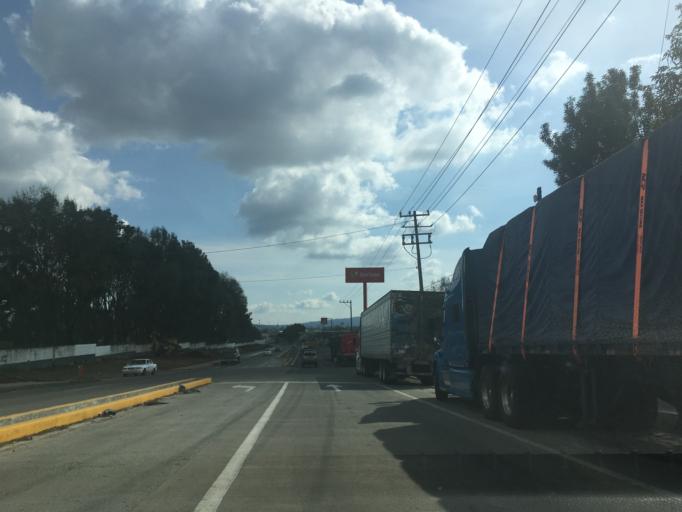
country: MX
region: Michoacan
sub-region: Uruapan
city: Toreo Bajo (El Toreo Bajo)
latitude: 19.4280
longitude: -102.0252
